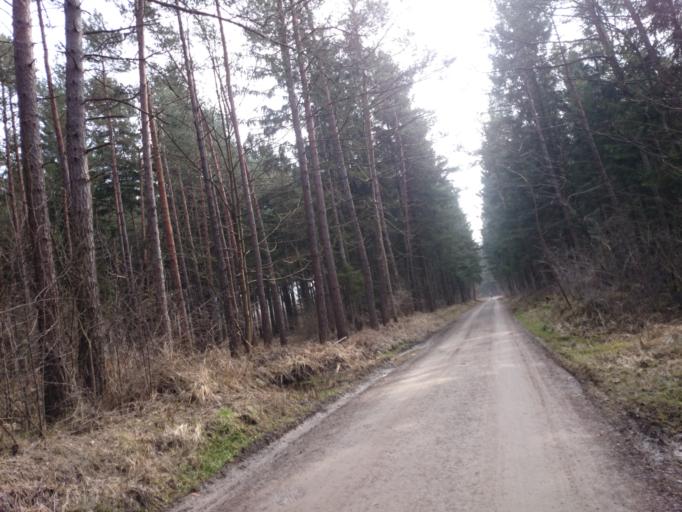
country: DE
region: Bavaria
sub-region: Swabia
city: Konigsbrunn
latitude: 48.2826
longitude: 10.9143
